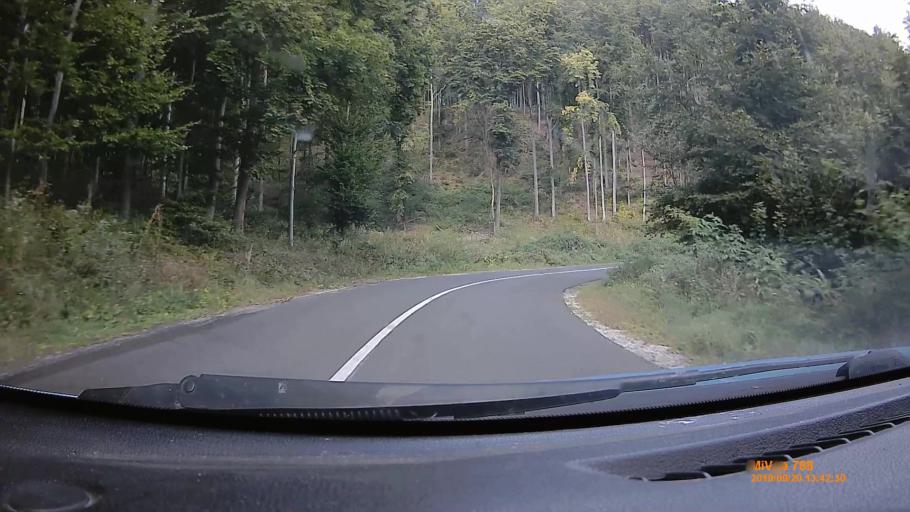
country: HU
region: Heves
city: Szilvasvarad
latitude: 48.0583
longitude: 20.5456
